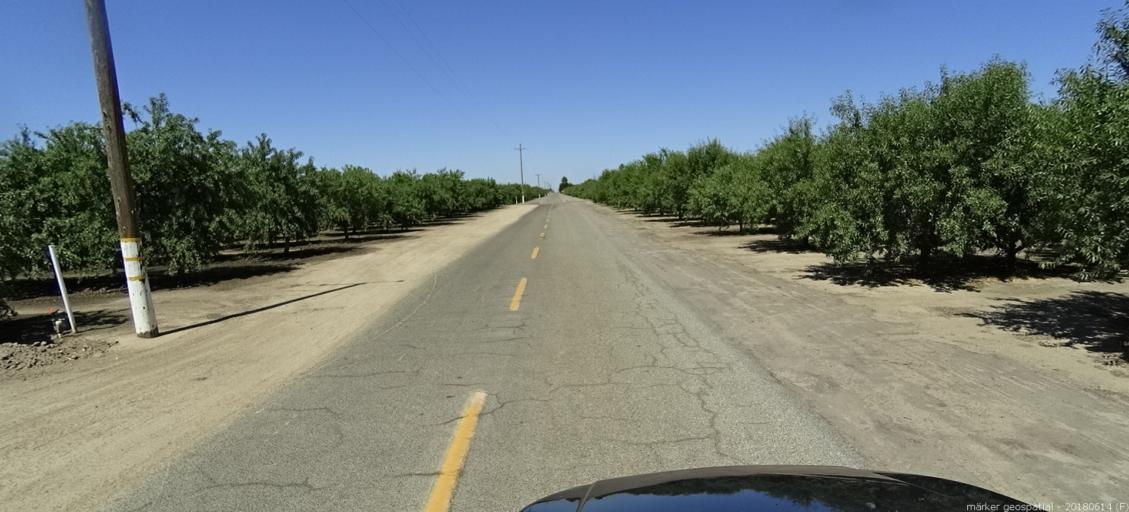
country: US
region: California
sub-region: Madera County
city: Fairmead
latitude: 36.9892
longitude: -120.1965
